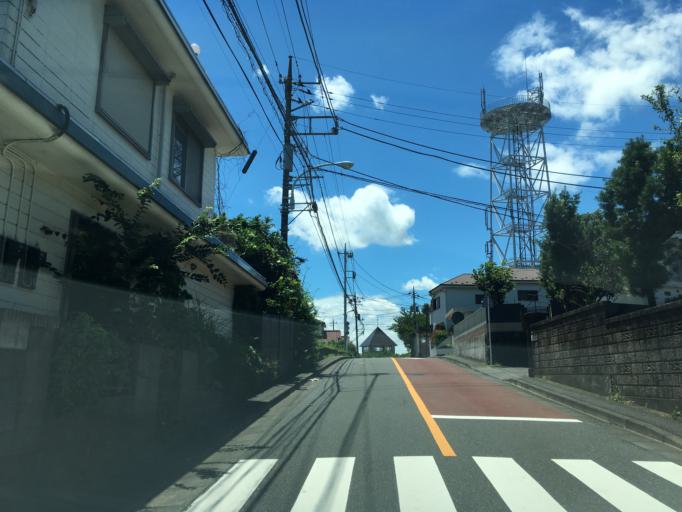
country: JP
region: Tokyo
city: Kokubunji
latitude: 35.6325
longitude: 139.4656
